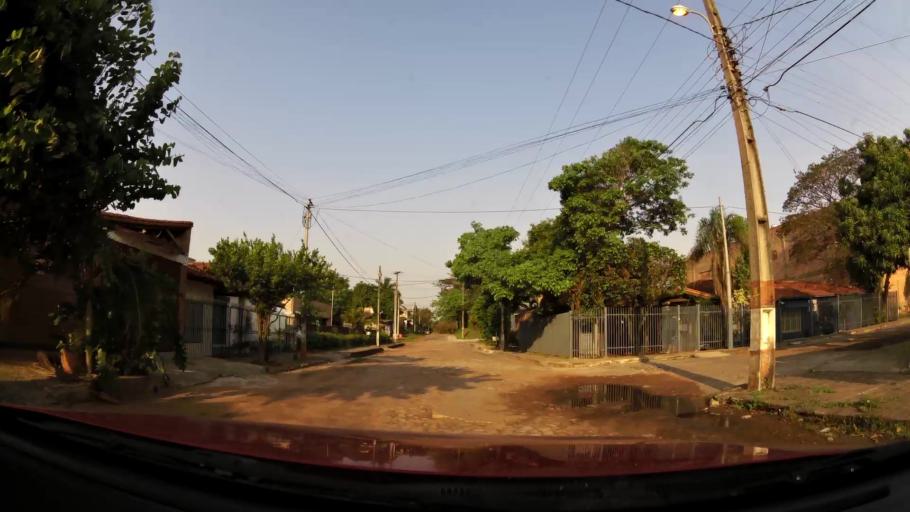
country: PY
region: Central
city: Lambare
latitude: -25.3477
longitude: -57.6087
